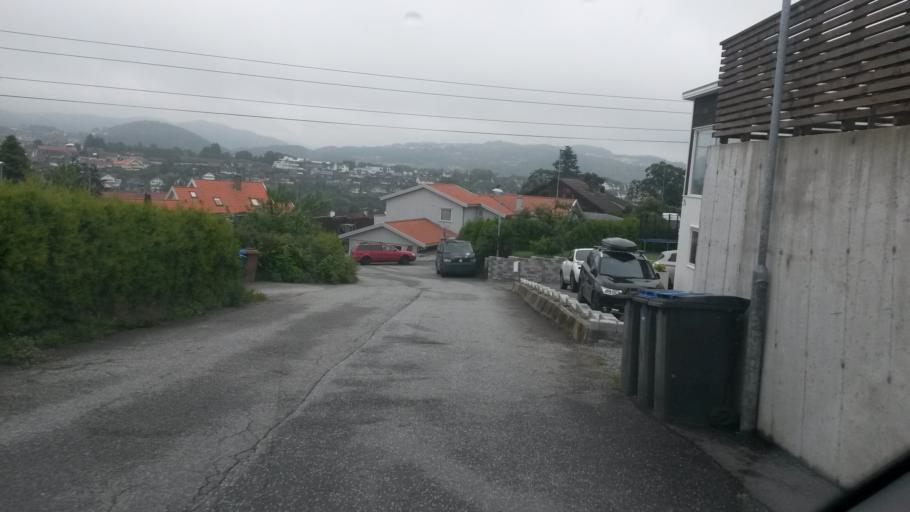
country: NO
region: Rogaland
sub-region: Sandnes
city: Sandnes
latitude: 58.8314
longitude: 5.7132
